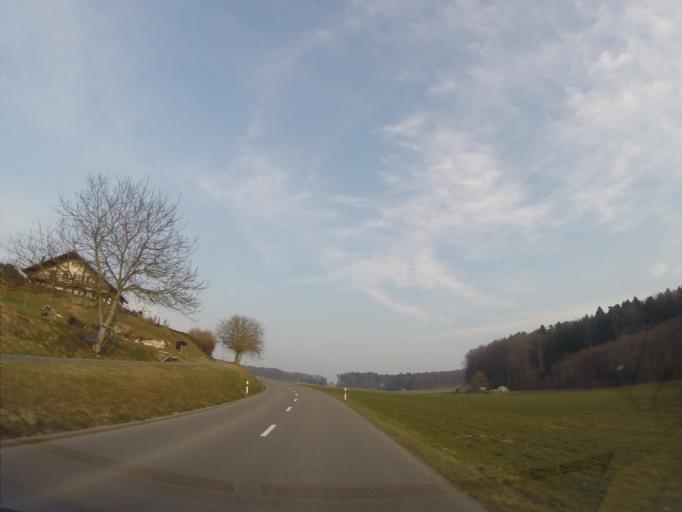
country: CH
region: Zurich
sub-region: Bezirk Andelfingen
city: Kleinandelfingen
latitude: 47.6373
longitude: 8.7000
